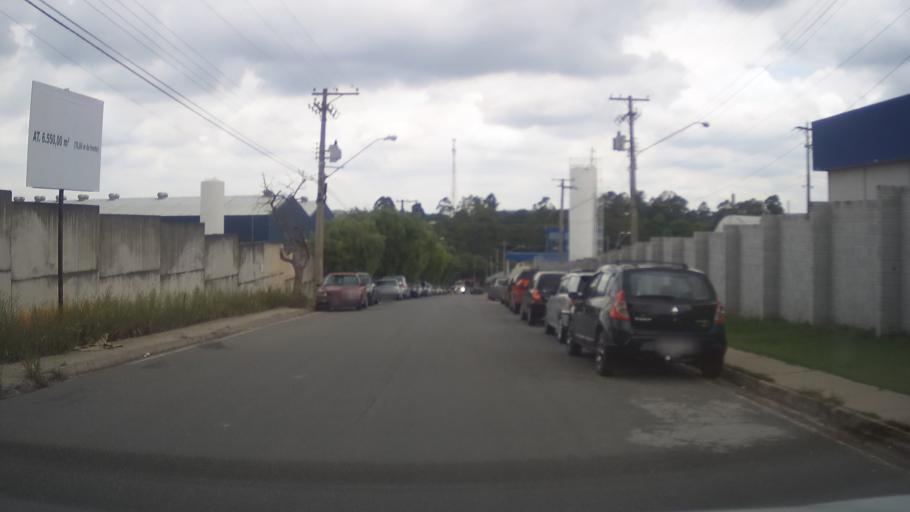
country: BR
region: Sao Paulo
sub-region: Itupeva
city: Itupeva
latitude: -23.1643
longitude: -47.0088
